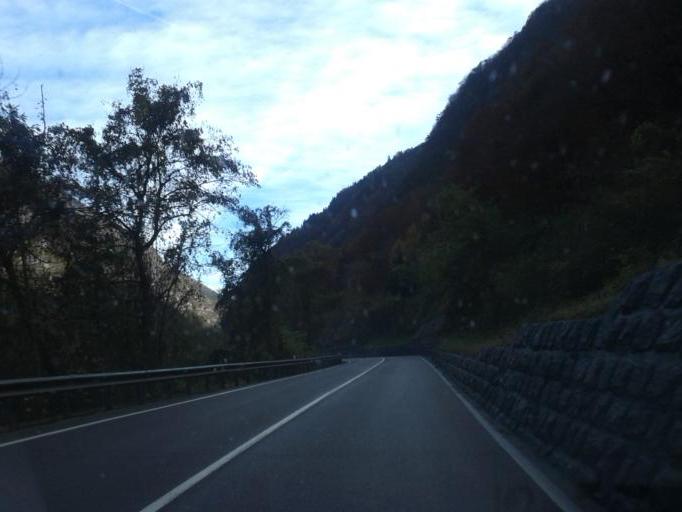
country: IT
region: Trentino-Alto Adige
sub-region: Provincia di Trento
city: Ragoli
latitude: 46.0526
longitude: 10.8092
